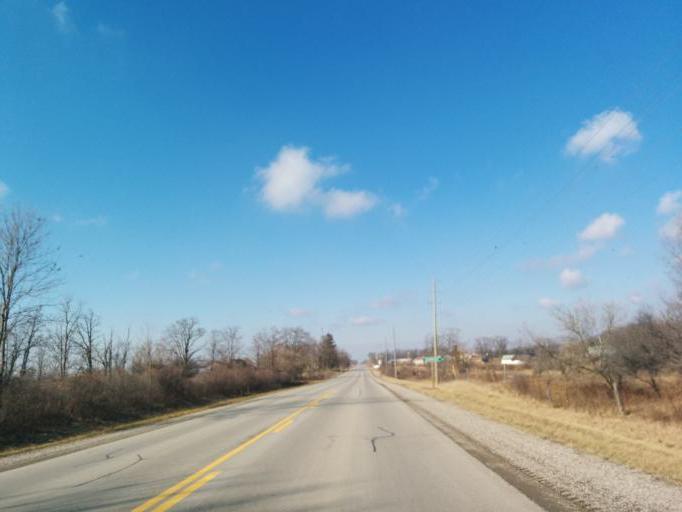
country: CA
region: Ontario
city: Brantford
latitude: 43.0025
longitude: -80.1615
